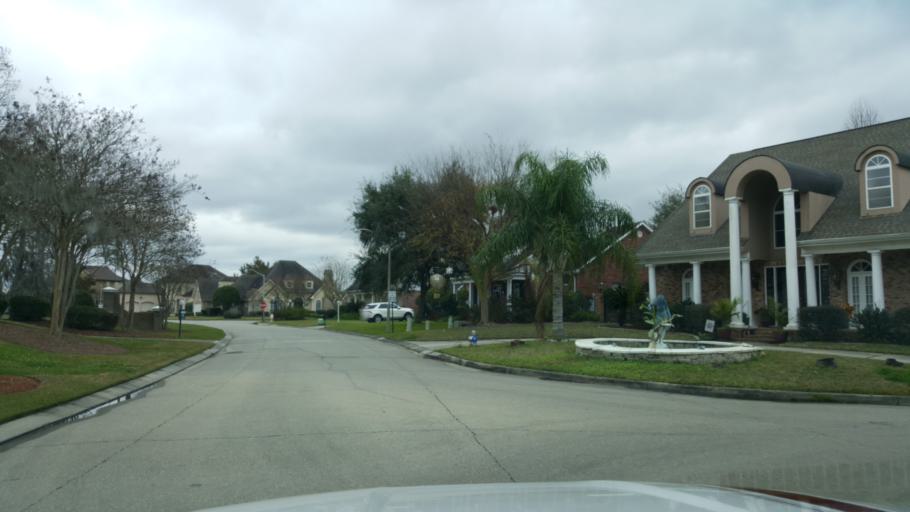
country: US
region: Louisiana
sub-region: Jefferson Parish
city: Woodmere
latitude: 29.8729
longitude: -90.0782
